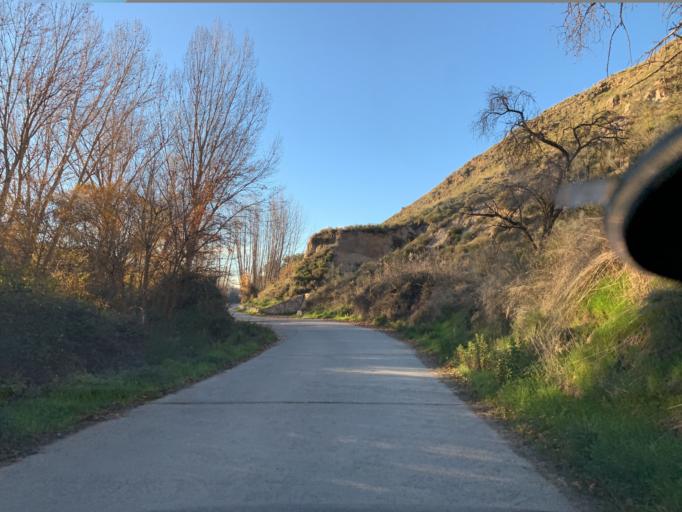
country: ES
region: Andalusia
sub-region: Provincia de Granada
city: Dilar
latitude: 37.0679
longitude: -3.5758
